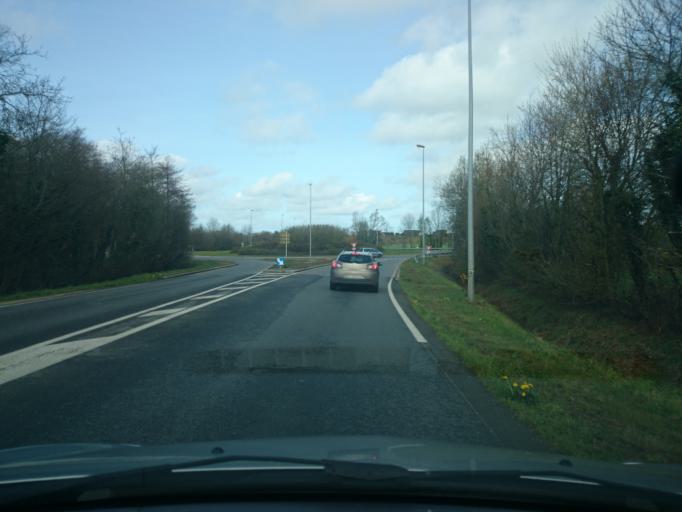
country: FR
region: Brittany
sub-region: Departement du Finistere
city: Gouesnou
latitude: 48.4431
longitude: -4.4553
